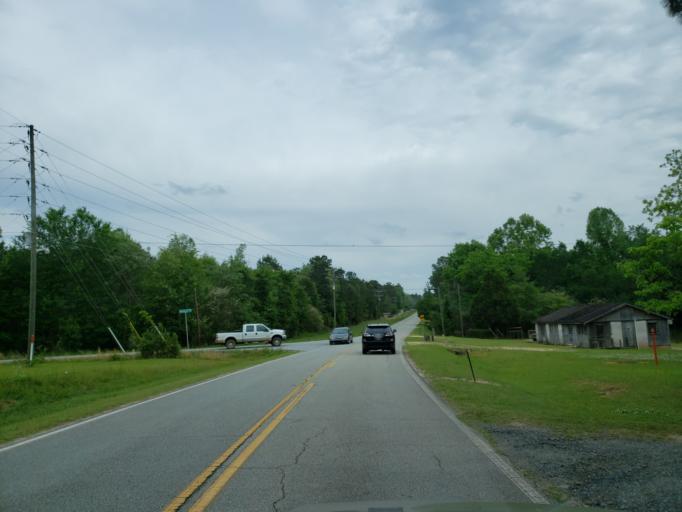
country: US
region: Georgia
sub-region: Bibb County
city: West Point
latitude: 32.8149
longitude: -83.8520
